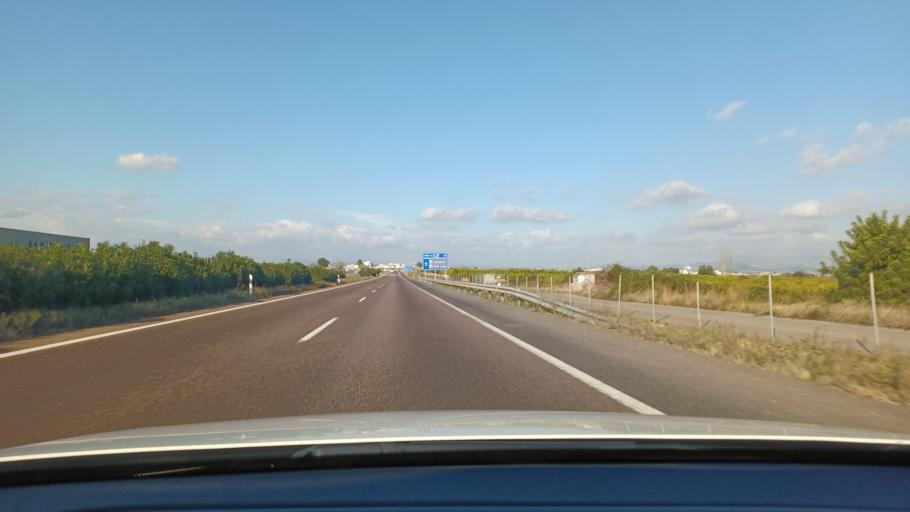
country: ES
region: Valencia
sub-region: Provincia de Castello
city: Betxi
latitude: 39.9108
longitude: -0.1954
